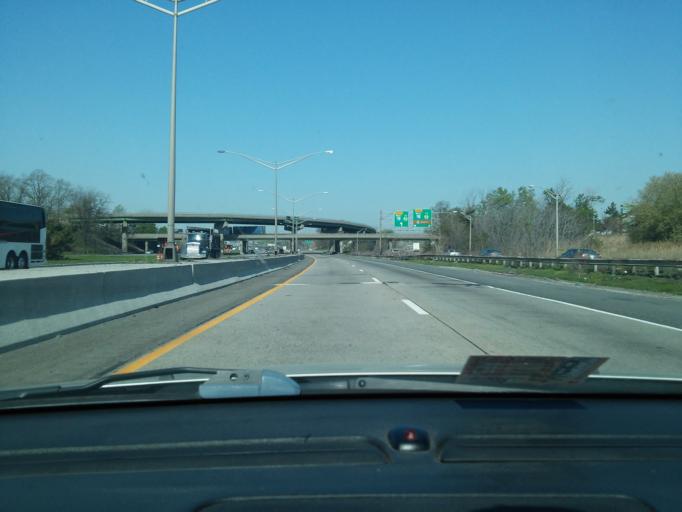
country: US
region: New Jersey
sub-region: Essex County
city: Newark
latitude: 40.7105
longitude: -74.1637
